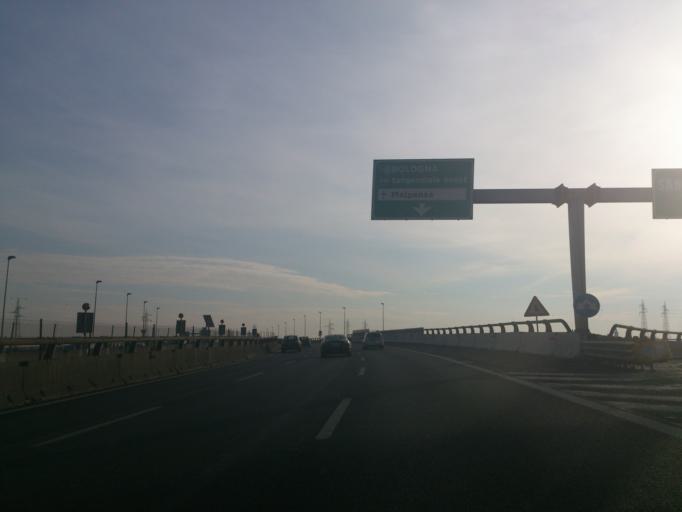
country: IT
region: Lombardy
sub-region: Citta metropolitana di Milano
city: Chiaravalle
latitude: 45.4263
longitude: 9.2455
